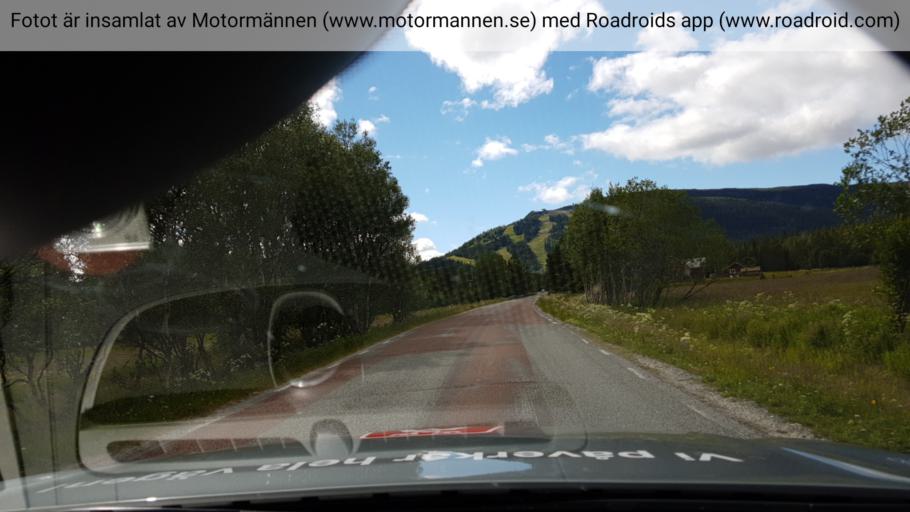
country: SE
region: Jaemtland
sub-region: Are Kommun
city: Are
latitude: 62.5495
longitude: 12.5998
